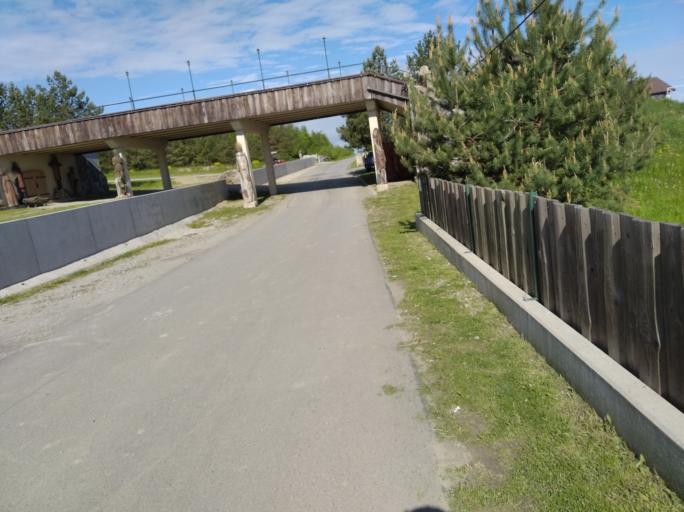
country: PL
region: Subcarpathian Voivodeship
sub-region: Powiat strzyzowski
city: Frysztak
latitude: 49.8366
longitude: 21.5222
